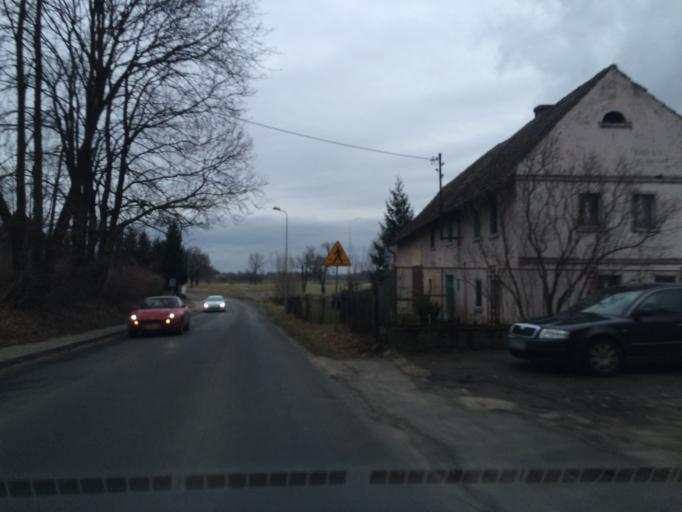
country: PL
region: Lower Silesian Voivodeship
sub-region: Powiat lubanski
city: Luban
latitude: 51.1625
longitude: 15.3183
